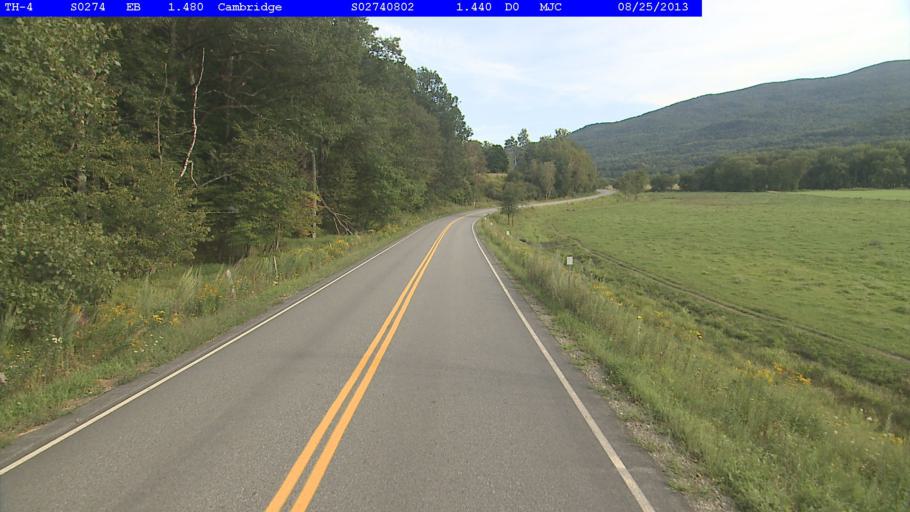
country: US
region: Vermont
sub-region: Lamoille County
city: Johnson
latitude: 44.6645
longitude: -72.7597
